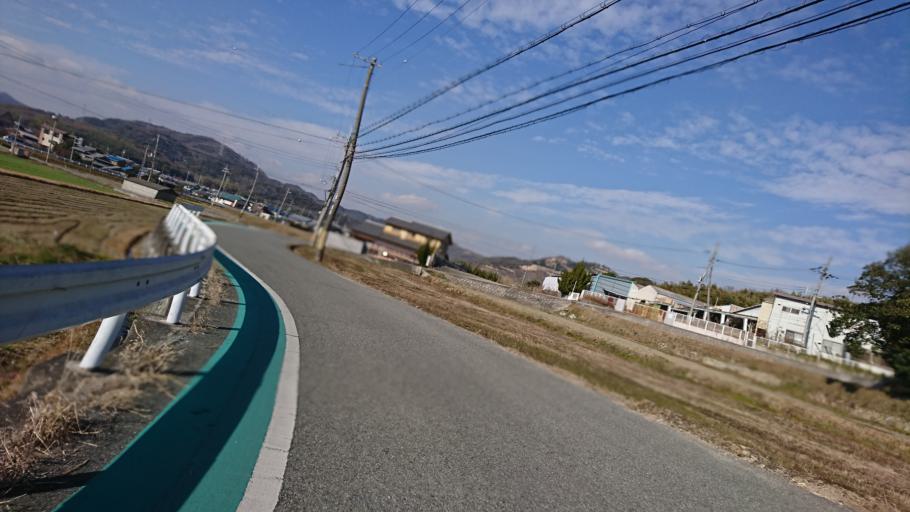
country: JP
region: Hyogo
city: Kakogawacho-honmachi
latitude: 34.8321
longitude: 134.8417
